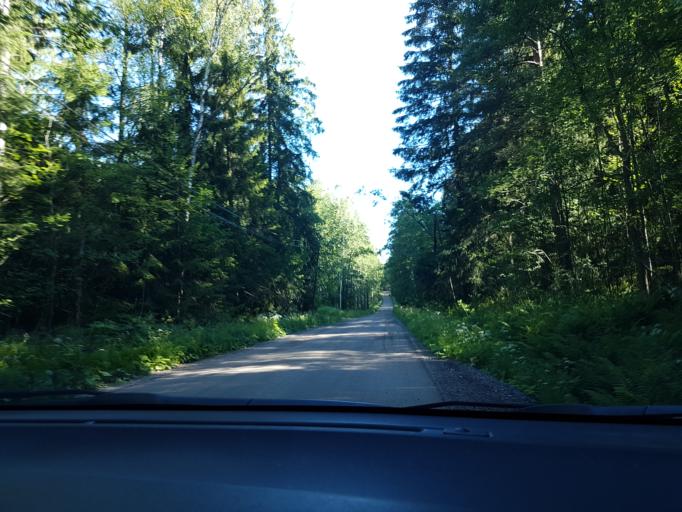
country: FI
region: Uusimaa
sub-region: Helsinki
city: Sibbo
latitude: 60.2659
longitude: 25.2280
